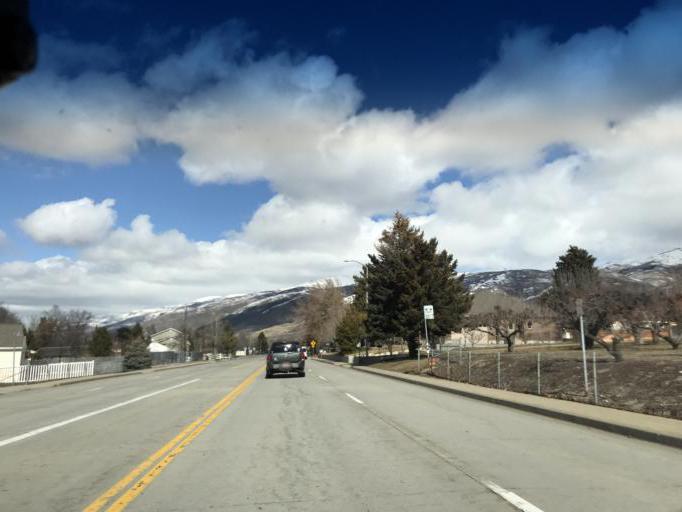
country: US
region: Utah
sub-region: Davis County
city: Woods Cross
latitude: 40.8730
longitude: -111.8758
